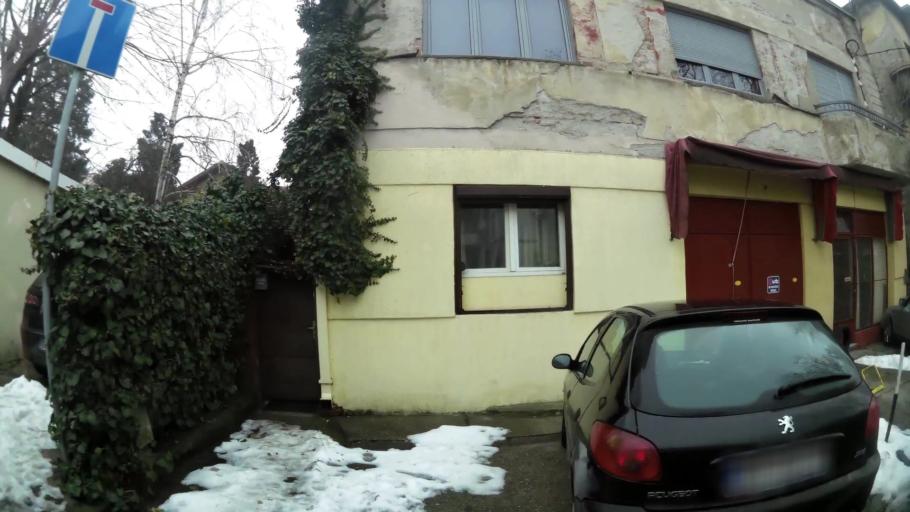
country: RS
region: Central Serbia
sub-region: Belgrade
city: Savski Venac
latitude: 44.7956
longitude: 20.4474
